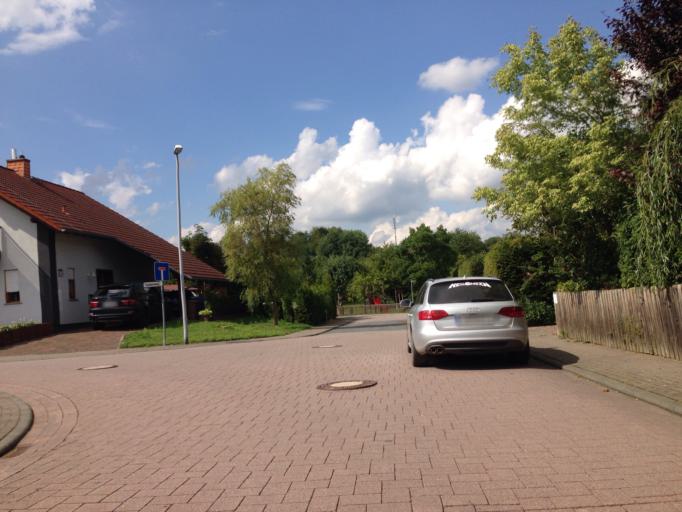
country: DE
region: Hesse
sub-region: Regierungsbezirk Giessen
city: Lohnberg
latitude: 50.5141
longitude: 8.2634
